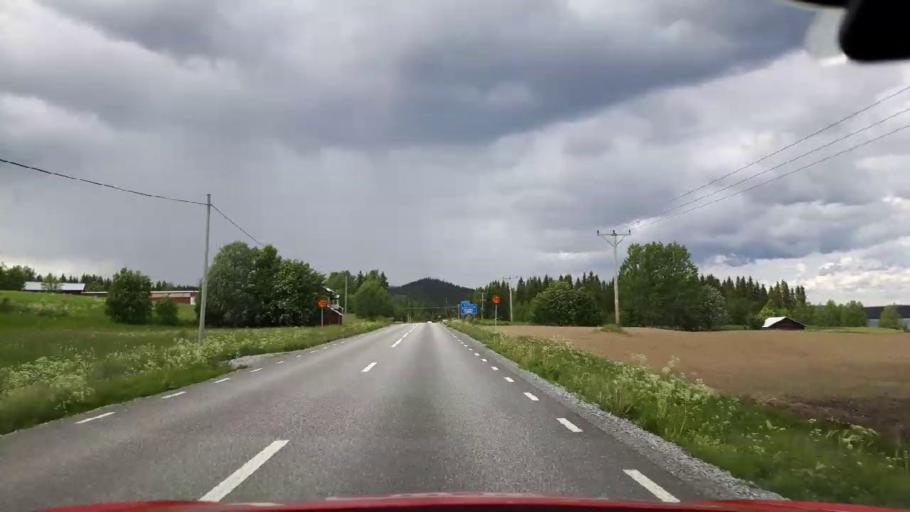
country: SE
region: Jaemtland
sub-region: Krokoms Kommun
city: Krokom
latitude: 63.6806
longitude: 14.3340
